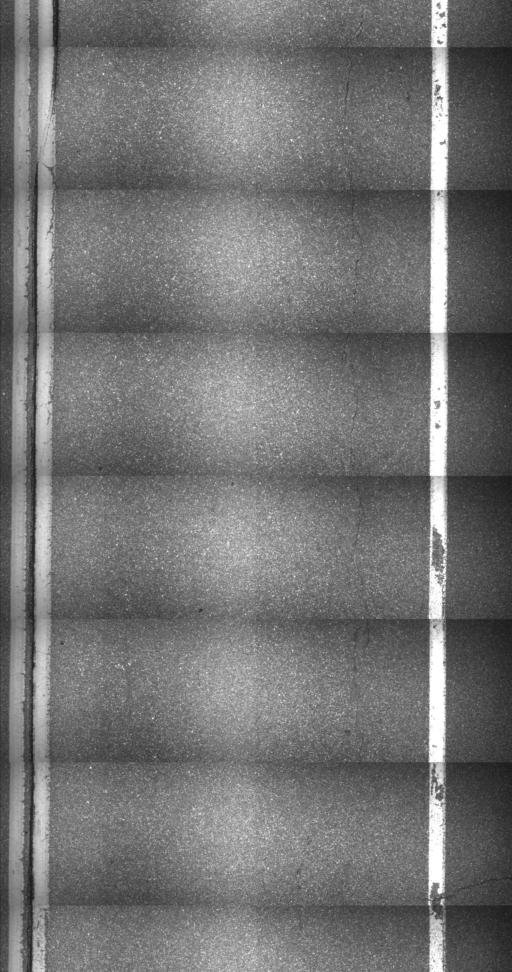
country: US
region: Vermont
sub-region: Lamoille County
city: Johnson
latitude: 44.6084
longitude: -72.8115
